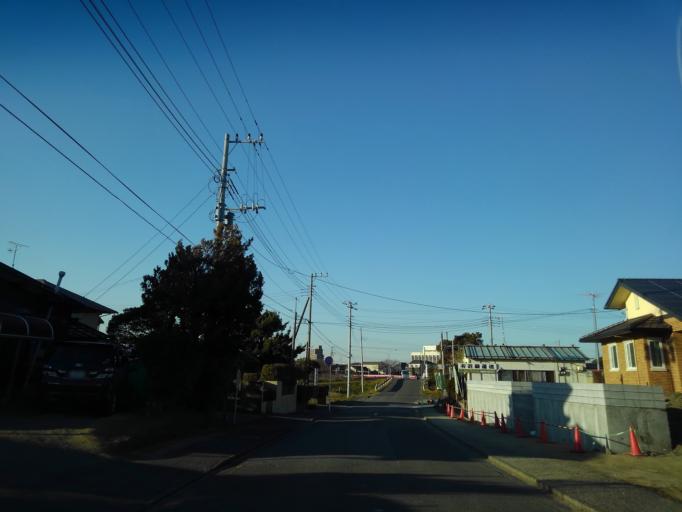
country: JP
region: Chiba
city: Kimitsu
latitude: 35.3233
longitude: 139.9046
